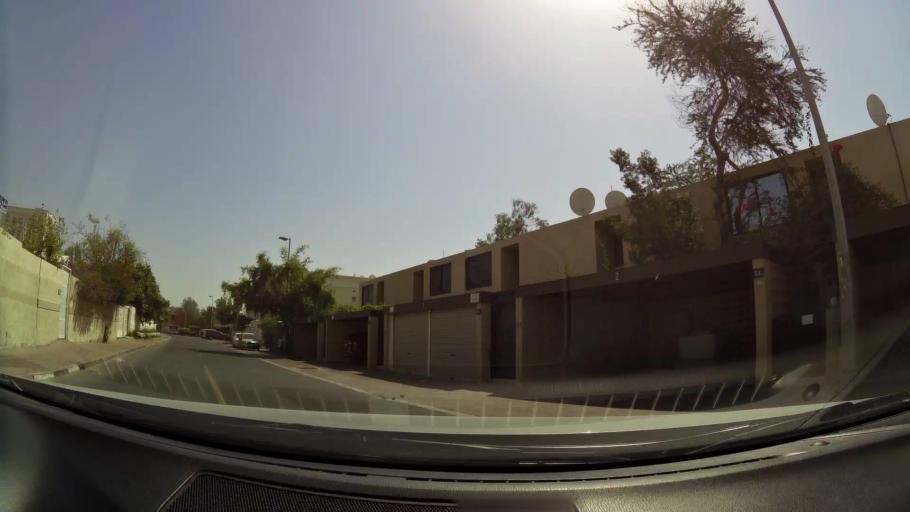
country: AE
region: Ash Shariqah
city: Sharjah
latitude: 25.2330
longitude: 55.2722
